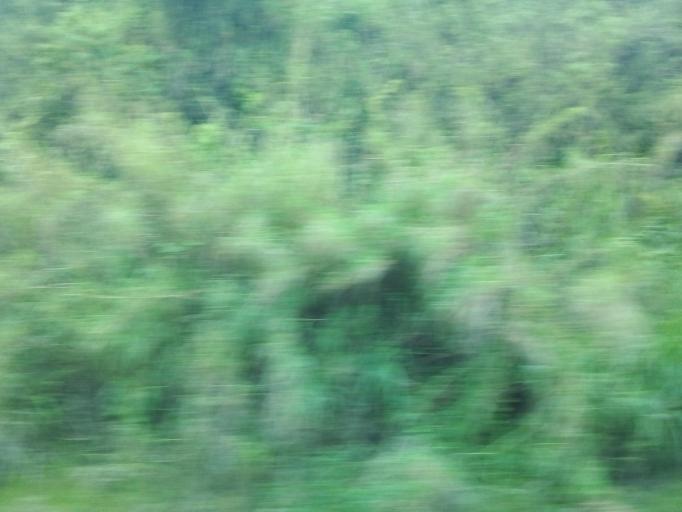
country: BR
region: Minas Gerais
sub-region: Rio Piracicaba
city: Rio Piracicaba
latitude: -19.9724
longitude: -43.2078
